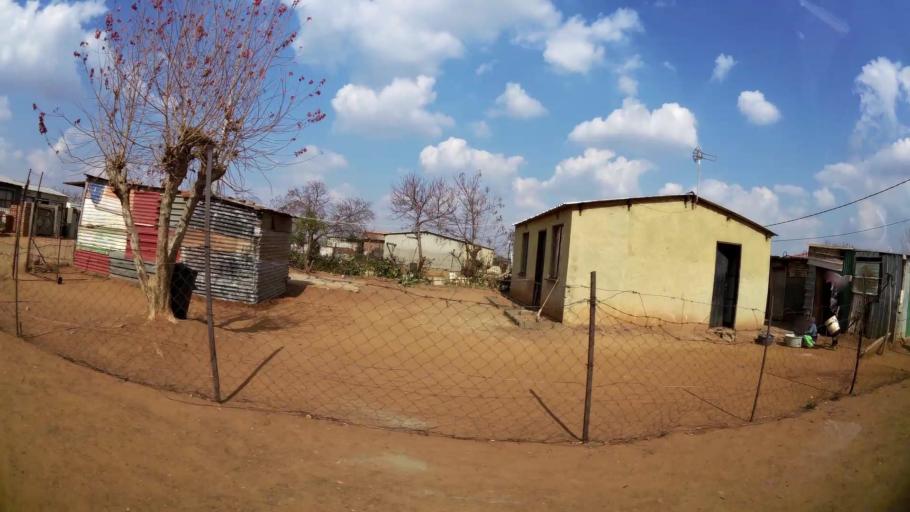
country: ZA
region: Gauteng
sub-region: Ekurhuleni Metropolitan Municipality
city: Springs
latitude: -26.1297
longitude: 28.4728
